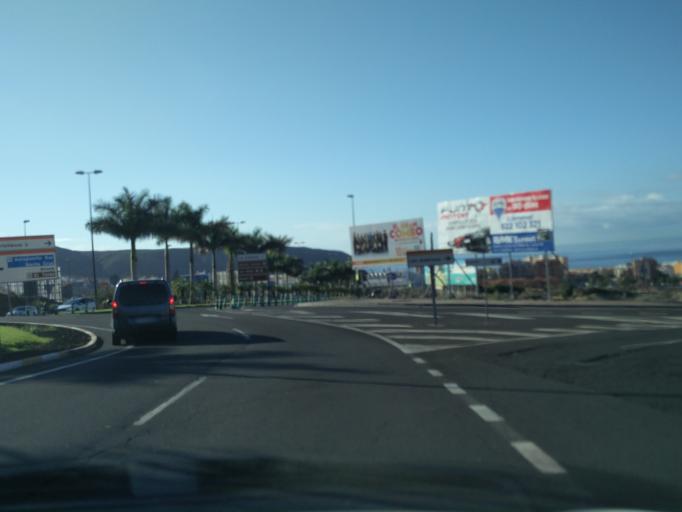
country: ES
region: Canary Islands
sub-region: Provincia de Santa Cruz de Tenerife
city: Playa de las Americas
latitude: 28.0631
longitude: -16.7113
